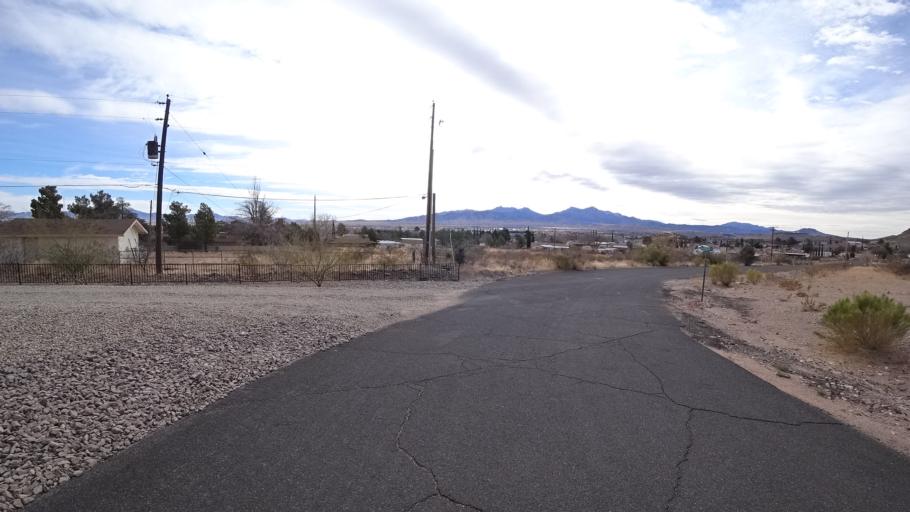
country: US
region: Arizona
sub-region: Mohave County
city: New Kingman-Butler
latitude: 35.2340
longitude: -114.0495
